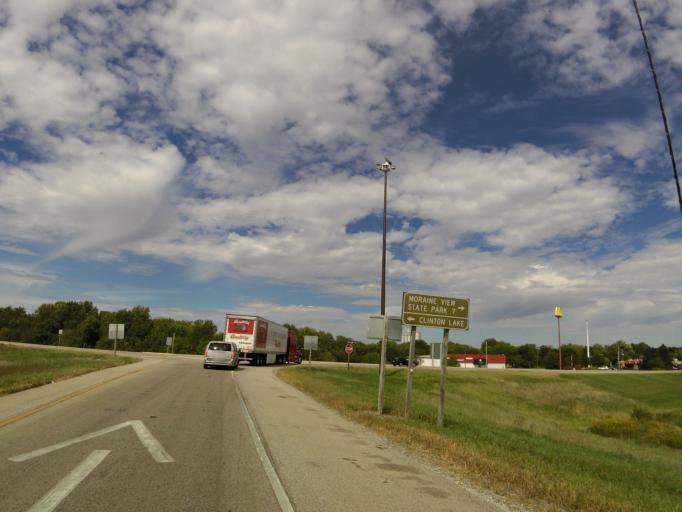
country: US
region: Illinois
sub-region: McLean County
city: Le Roy
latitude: 40.3397
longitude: -88.7631
